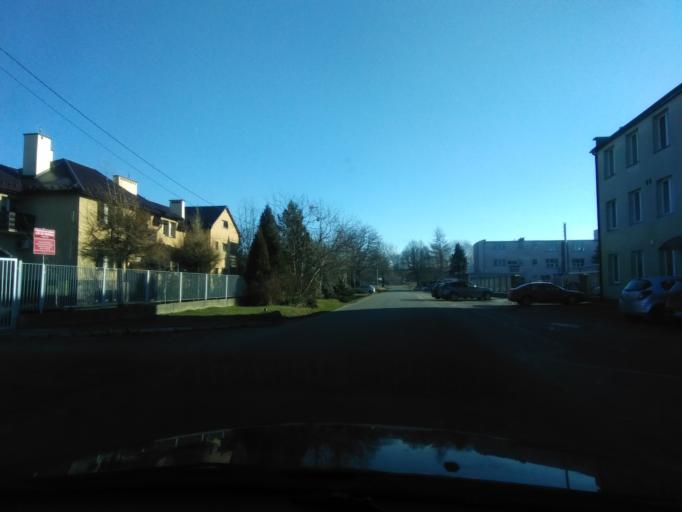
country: PL
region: Subcarpathian Voivodeship
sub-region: Powiat krosnienski
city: Rymanow
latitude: 49.5728
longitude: 21.8743
